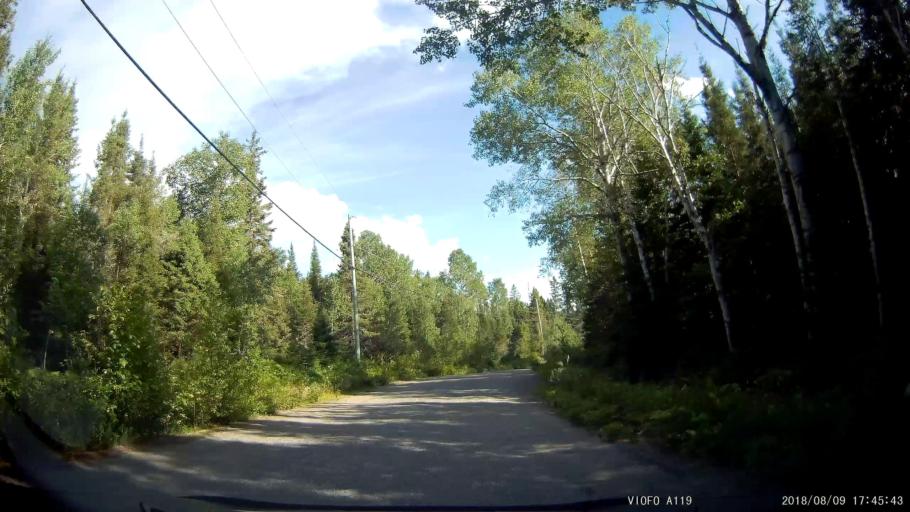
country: CA
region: Ontario
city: Rayside-Balfour
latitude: 46.5986
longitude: -81.5342
